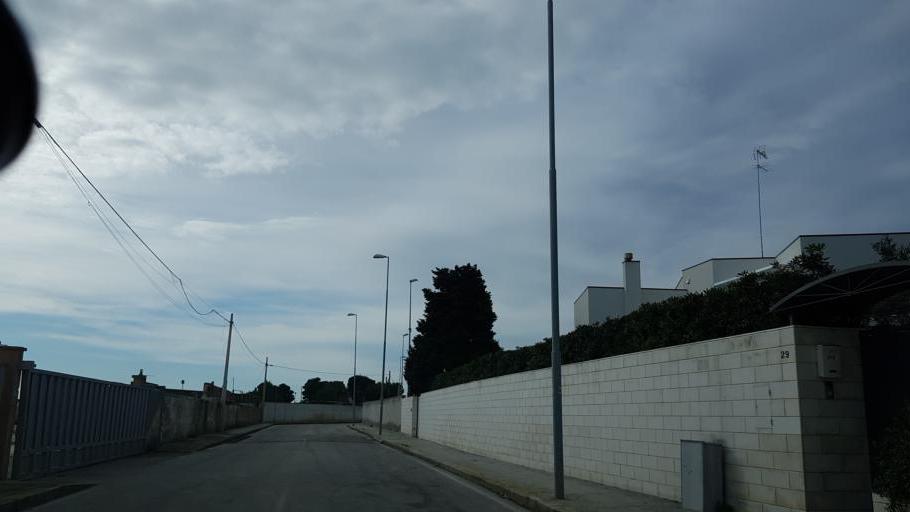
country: IT
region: Apulia
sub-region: Provincia di Brindisi
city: Materdomini
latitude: 40.6567
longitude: 17.9598
